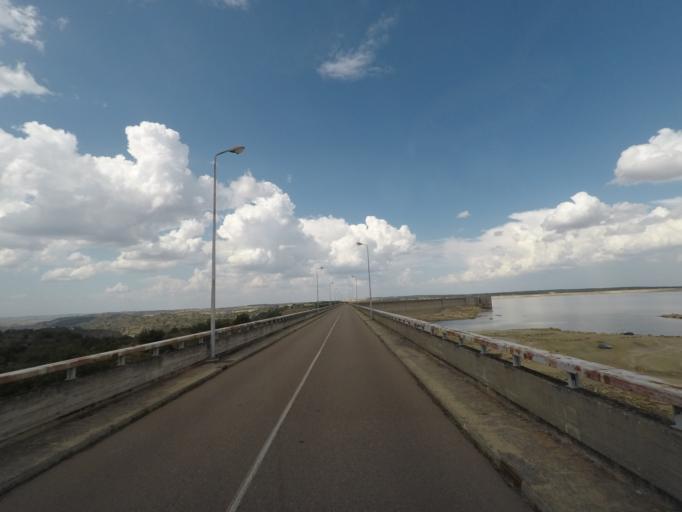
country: ES
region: Castille and Leon
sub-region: Provincia de Salamanca
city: Almendra
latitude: 41.2611
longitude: -6.3223
